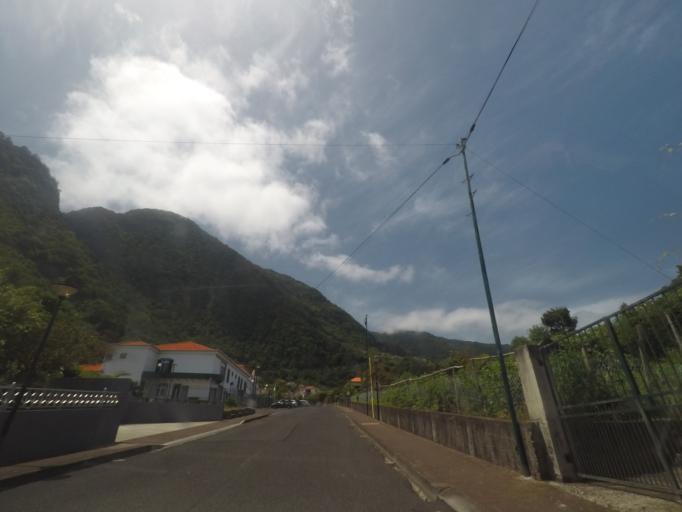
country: PT
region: Madeira
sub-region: Sao Vicente
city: Sao Vicente
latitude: 32.8251
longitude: -16.9887
